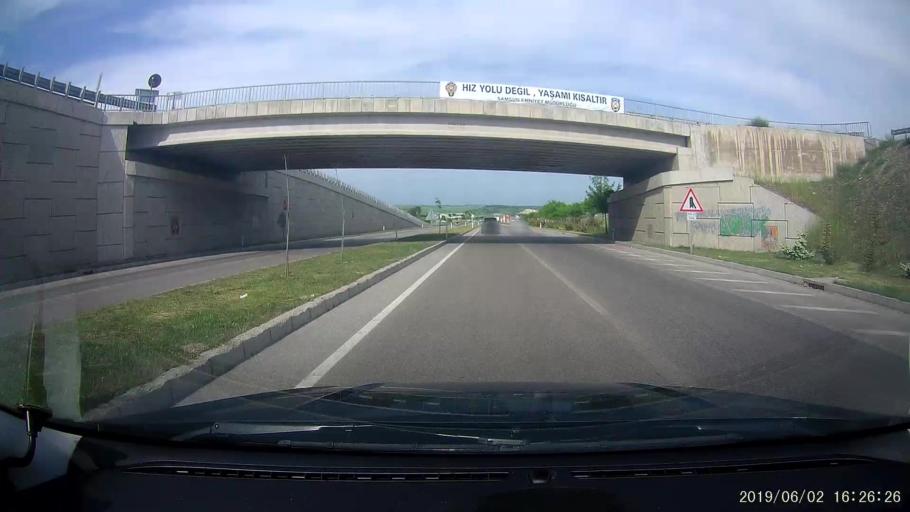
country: TR
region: Samsun
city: Ladik
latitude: 40.9997
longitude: 35.8022
